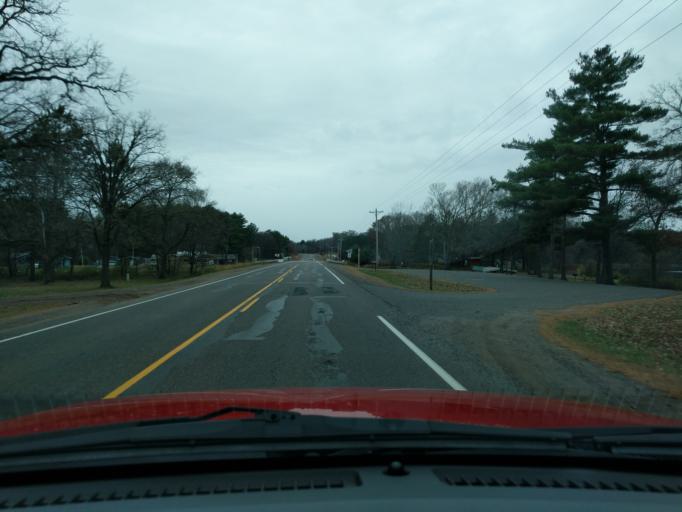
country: US
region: Wisconsin
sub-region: Burnett County
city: Siren
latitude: 45.8191
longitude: -92.3262
